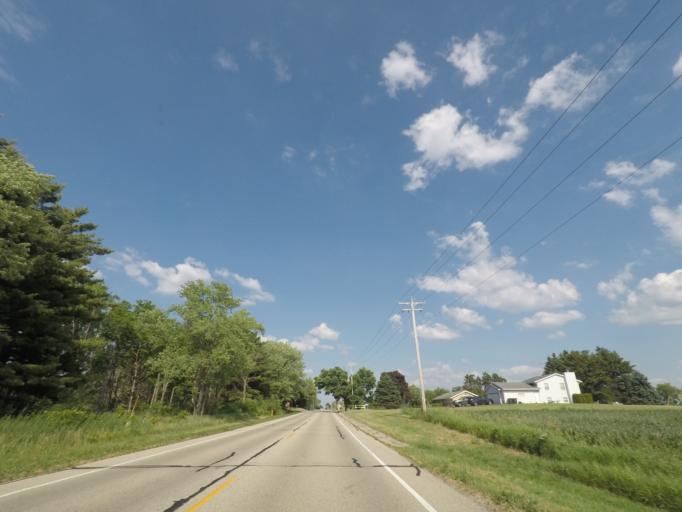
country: US
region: Wisconsin
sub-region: Walworth County
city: East Troy
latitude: 42.7930
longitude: -88.4774
